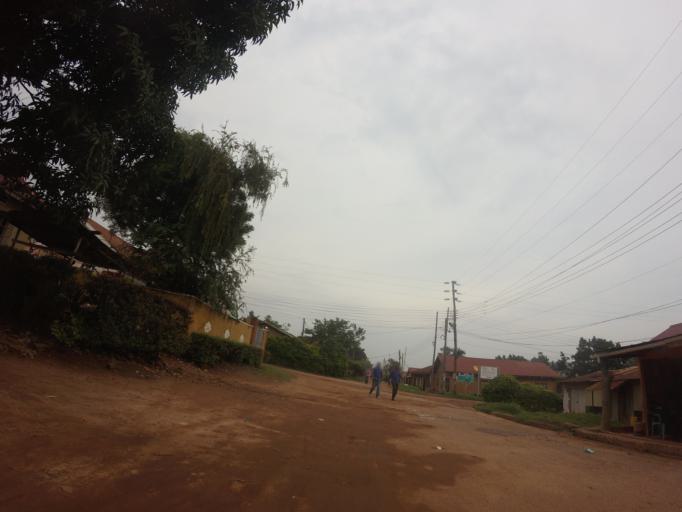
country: UG
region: Central Region
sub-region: Wakiso District
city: Kireka
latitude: 0.3420
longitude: 32.6189
